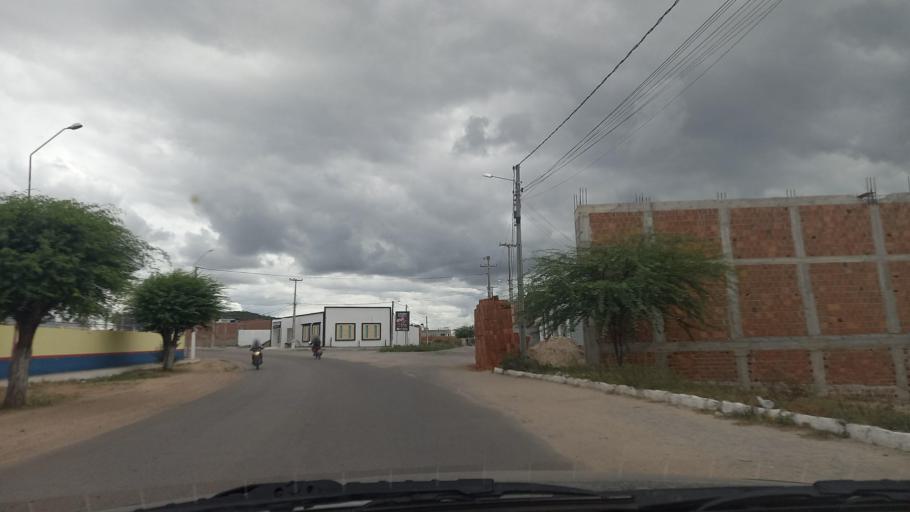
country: BR
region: Pernambuco
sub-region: Caruaru
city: Caruaru
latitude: -8.3265
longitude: -36.1425
